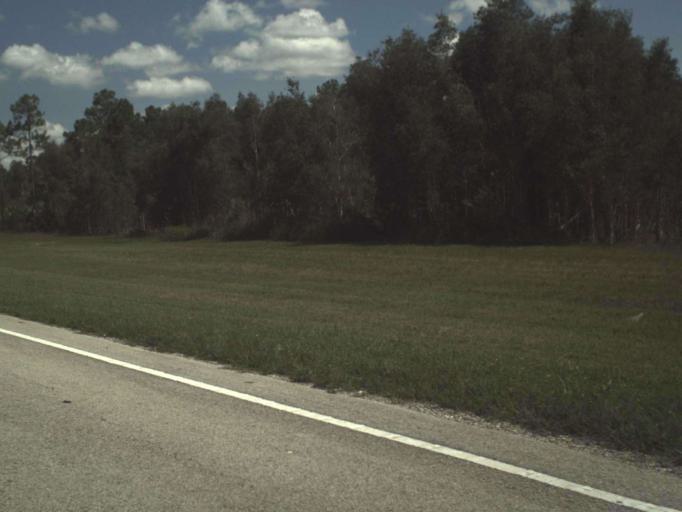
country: US
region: Florida
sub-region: Palm Beach County
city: Limestone Creek
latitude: 26.9019
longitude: -80.2879
